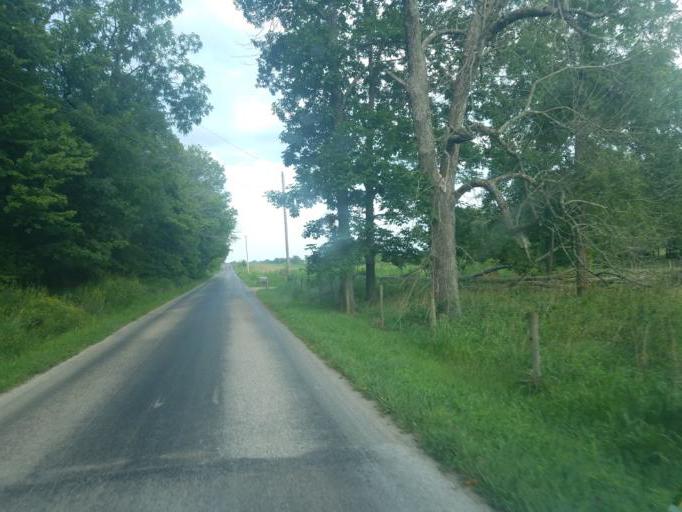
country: US
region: Ohio
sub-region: Knox County
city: Fredericktown
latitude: 40.5243
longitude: -82.6221
